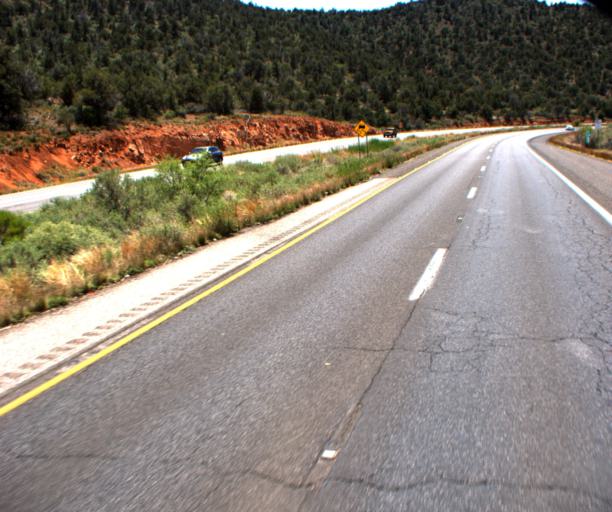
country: US
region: Arizona
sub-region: Yavapai County
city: West Sedona
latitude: 34.8467
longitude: -111.8384
